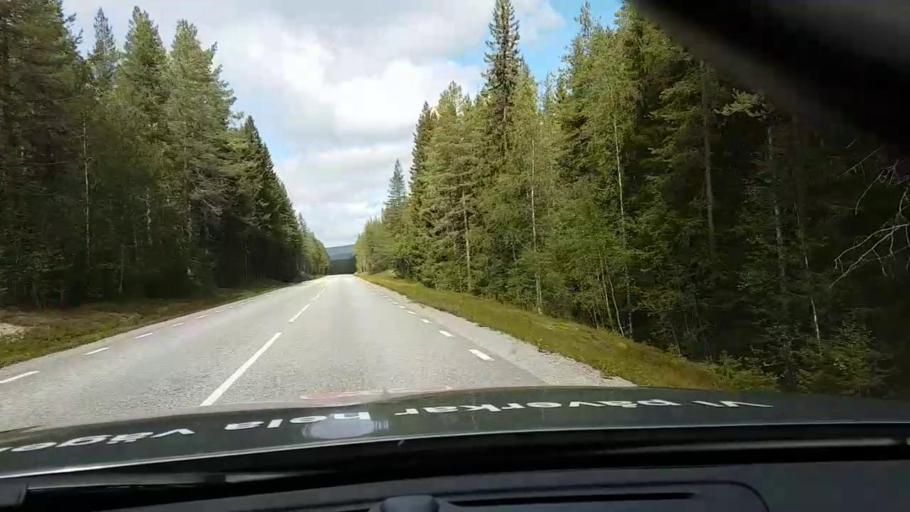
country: SE
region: Vaesternorrland
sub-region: OErnskoeldsviks Kommun
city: Bredbyn
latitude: 63.6972
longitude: 17.7642
